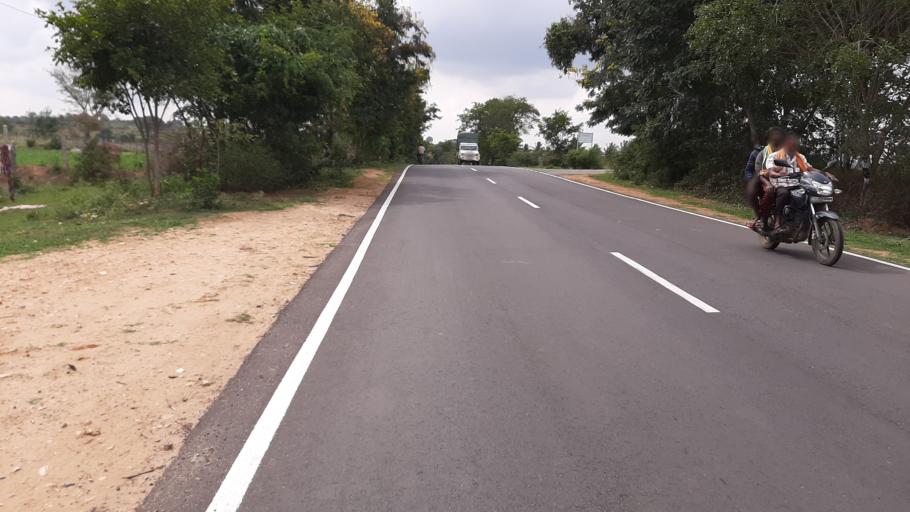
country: IN
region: Tamil Nadu
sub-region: Krishnagiri
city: Denkanikota
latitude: 12.5346
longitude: 77.7758
